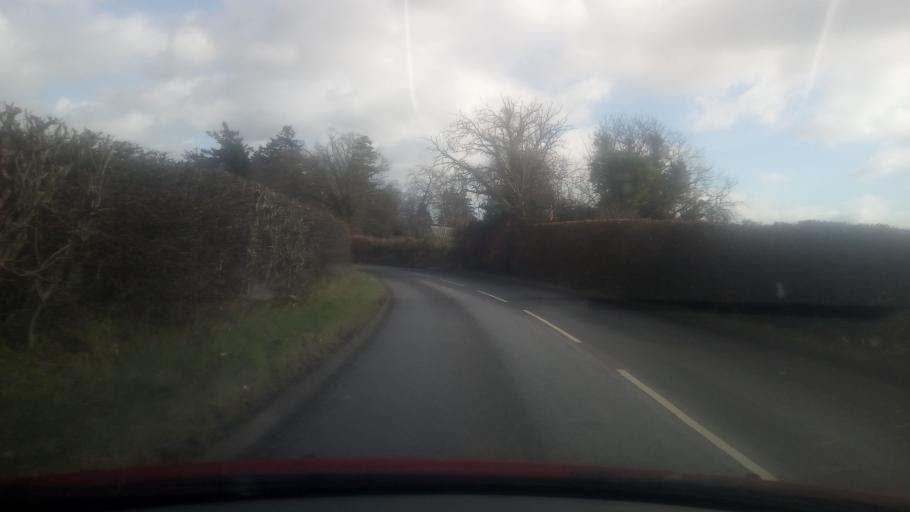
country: GB
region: Scotland
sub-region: The Scottish Borders
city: Saint Boswells
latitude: 55.5659
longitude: -2.6393
